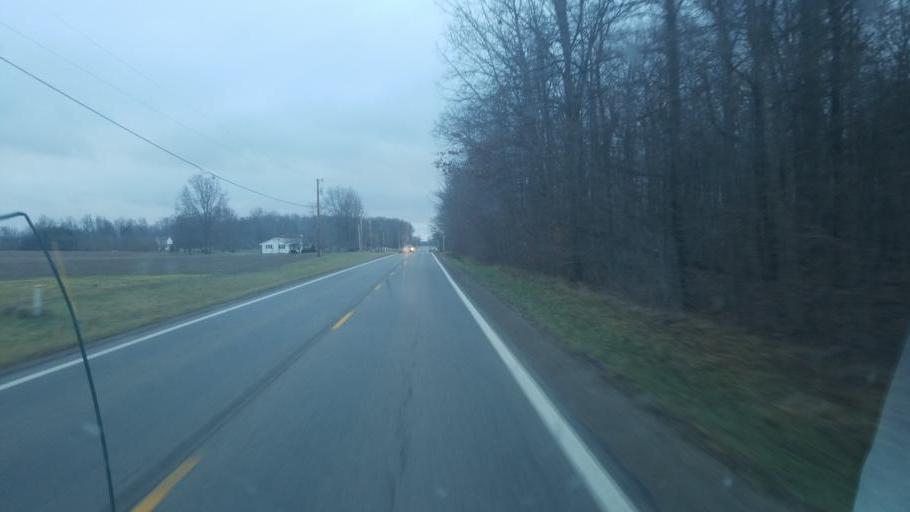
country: US
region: Ohio
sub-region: Crawford County
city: Galion
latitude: 40.6574
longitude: -82.7657
